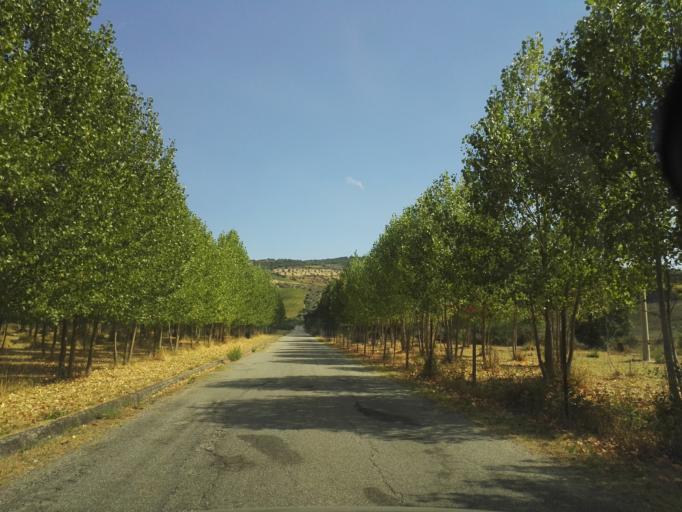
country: IT
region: Calabria
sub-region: Provincia di Reggio Calabria
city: Camini
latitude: 38.4515
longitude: 16.5015
